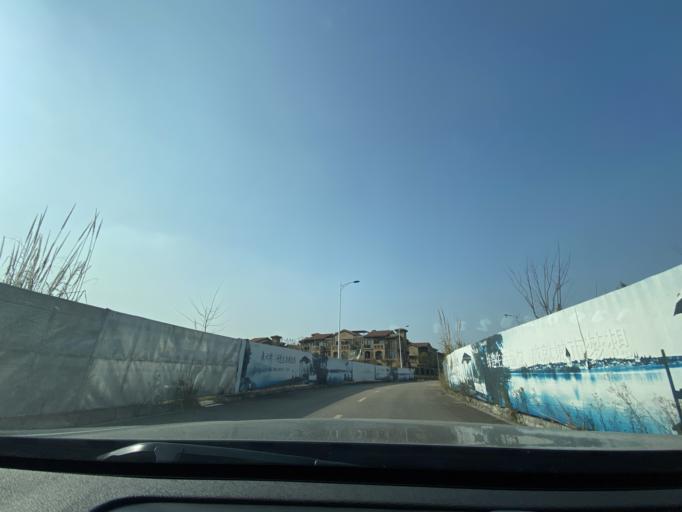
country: CN
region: Sichuan
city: Wenlin
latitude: 30.2522
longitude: 104.2467
